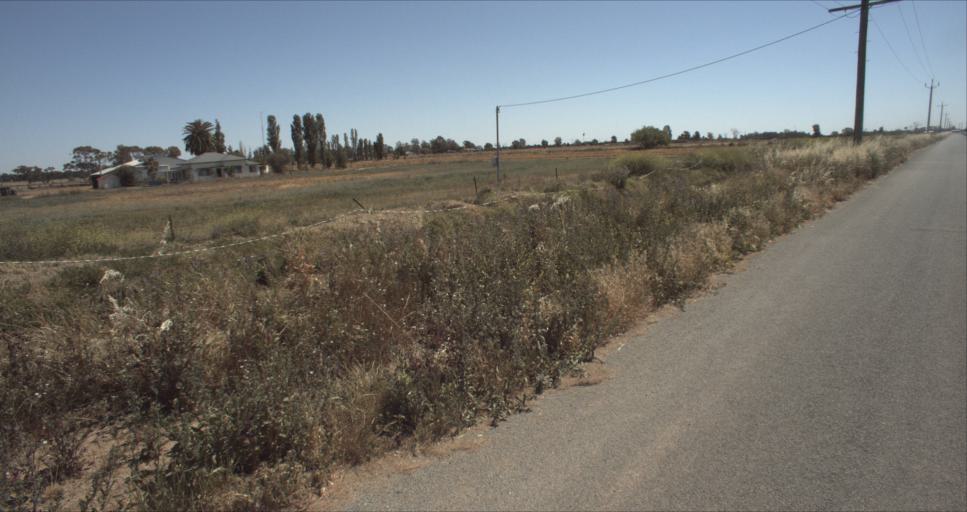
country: AU
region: New South Wales
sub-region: Leeton
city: Leeton
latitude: -34.5122
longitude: 146.4290
